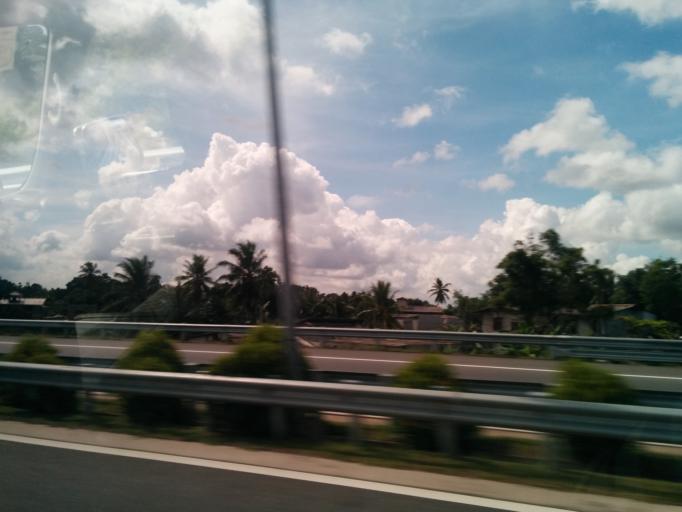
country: LK
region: Western
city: Wattala
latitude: 6.9774
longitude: 79.8978
